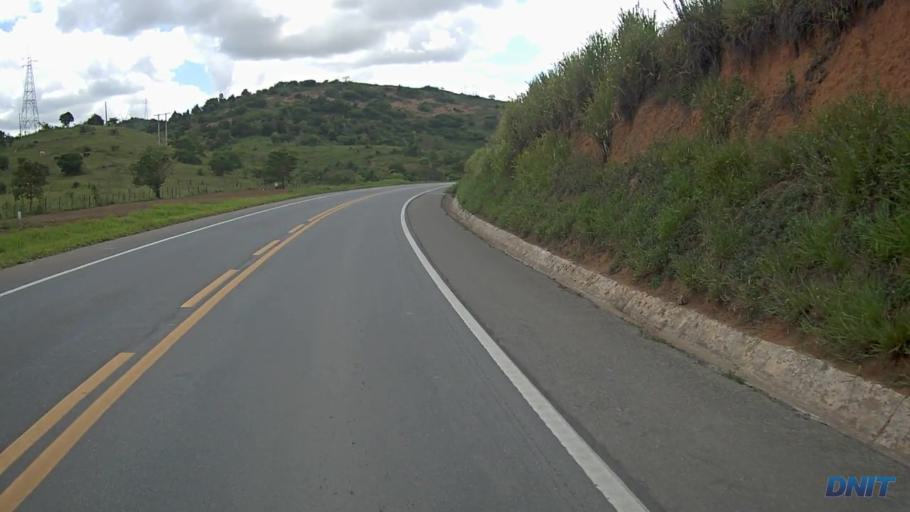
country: BR
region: Minas Gerais
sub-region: Governador Valadares
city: Governador Valadares
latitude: -18.9672
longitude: -42.0905
